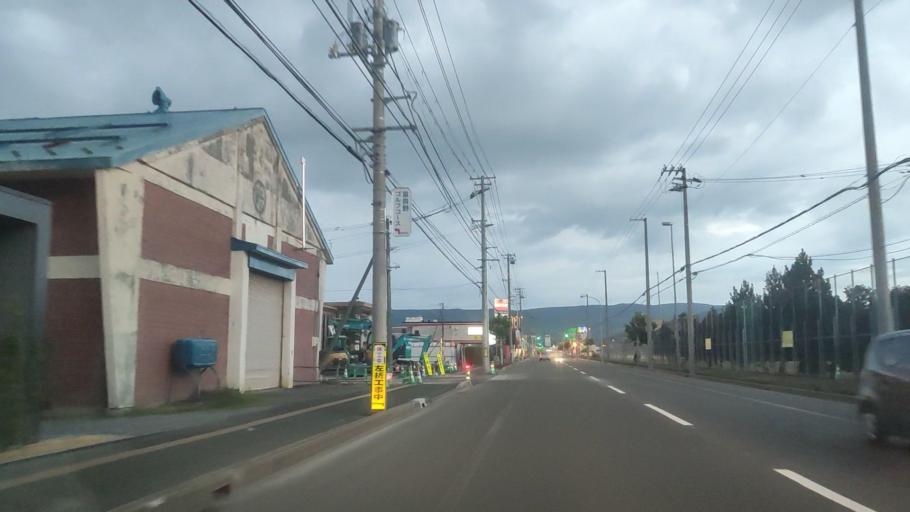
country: JP
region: Hokkaido
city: Shimo-furano
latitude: 43.3407
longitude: 142.3895
